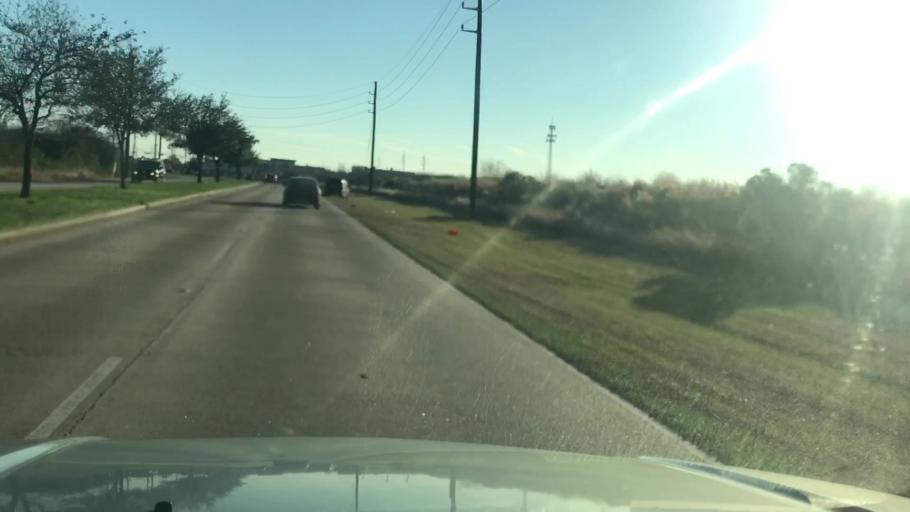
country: US
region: Texas
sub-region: Fort Bend County
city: Cinco Ranch
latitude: 29.8341
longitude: -95.7196
